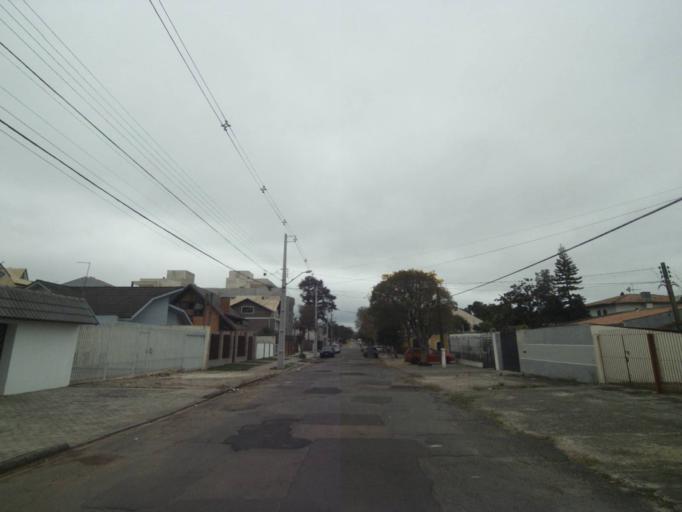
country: BR
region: Parana
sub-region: Curitiba
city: Curitiba
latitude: -25.4690
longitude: -49.2763
